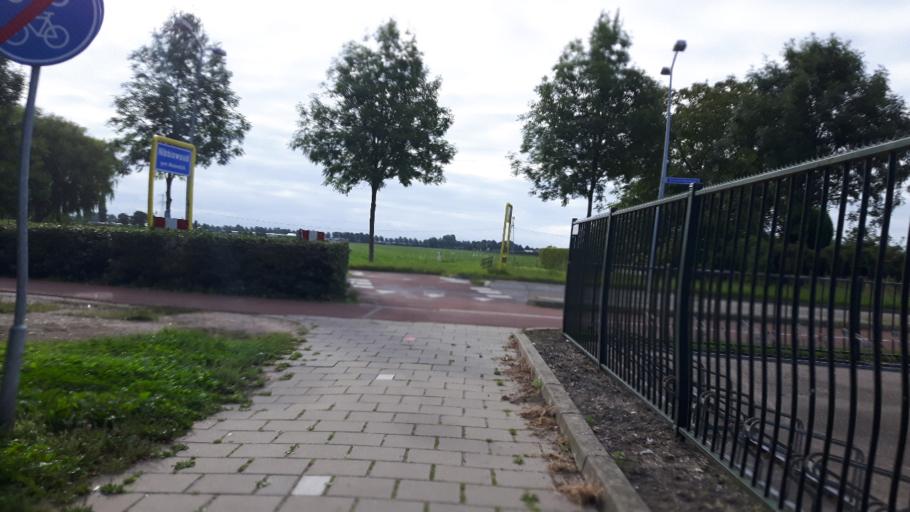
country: NL
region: North Holland
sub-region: Gemeente Hoorn
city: Hoorn
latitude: 52.6857
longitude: 5.0502
